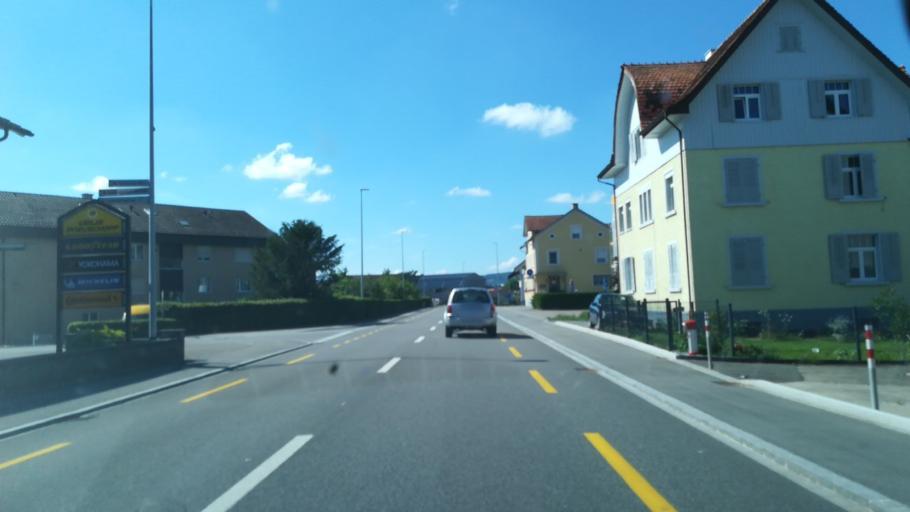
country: CH
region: Thurgau
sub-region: Weinfelden District
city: Sulgen
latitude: 47.5326
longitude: 9.1887
